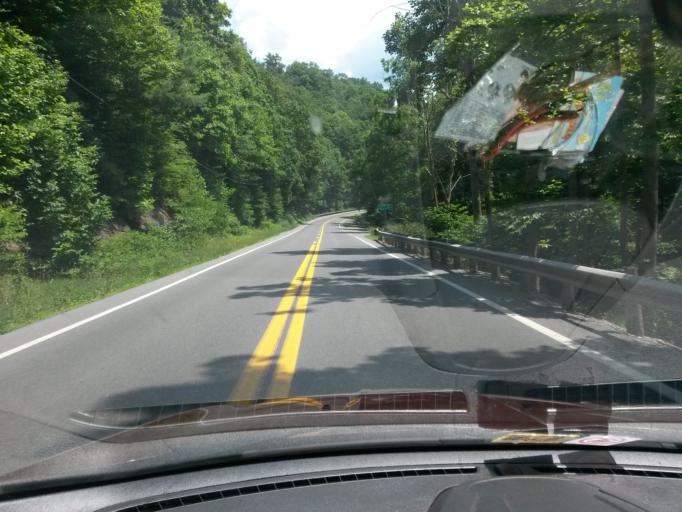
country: US
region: West Virginia
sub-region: Wyoming County
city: Pineville
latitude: 37.5600
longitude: -81.5410
